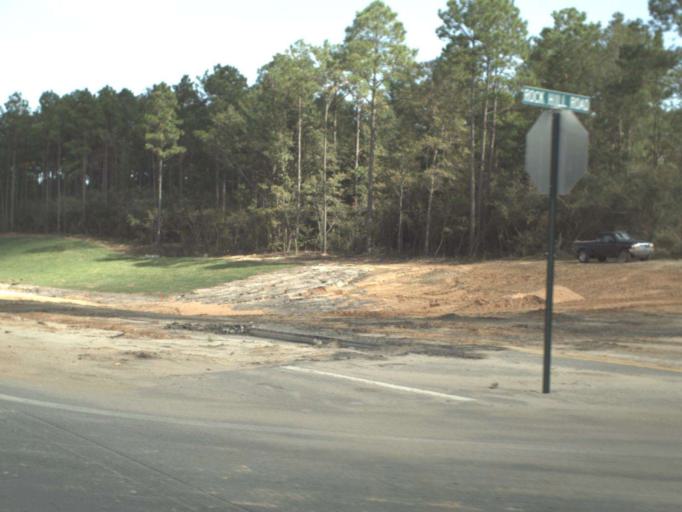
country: US
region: Florida
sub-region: Walton County
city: Freeport
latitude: 30.5987
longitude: -86.1108
